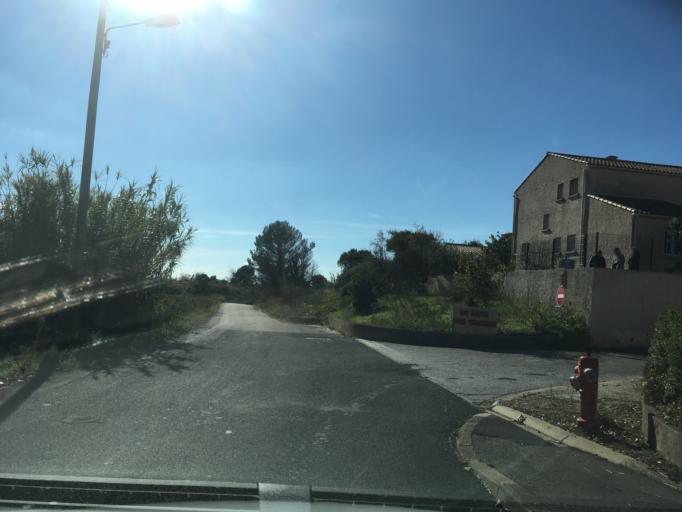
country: FR
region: Languedoc-Roussillon
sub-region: Departement de l'Herault
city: Juvignac
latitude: 43.6047
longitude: 3.8253
